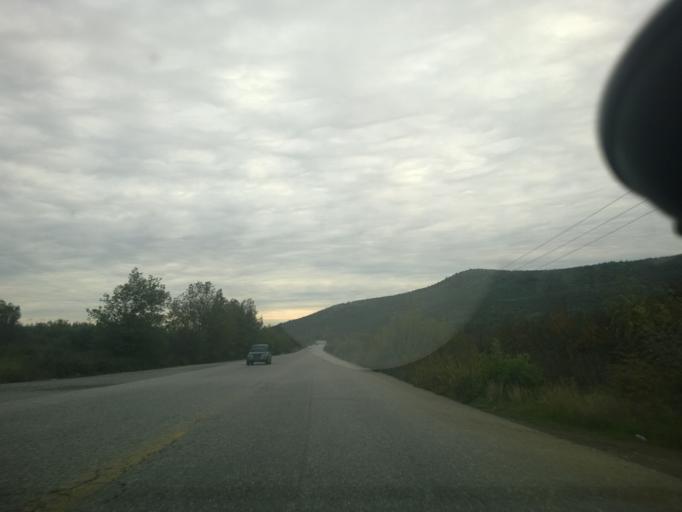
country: GR
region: Central Macedonia
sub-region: Nomos Pellis
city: Profitis Ilias
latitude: 40.8272
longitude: 22.1353
